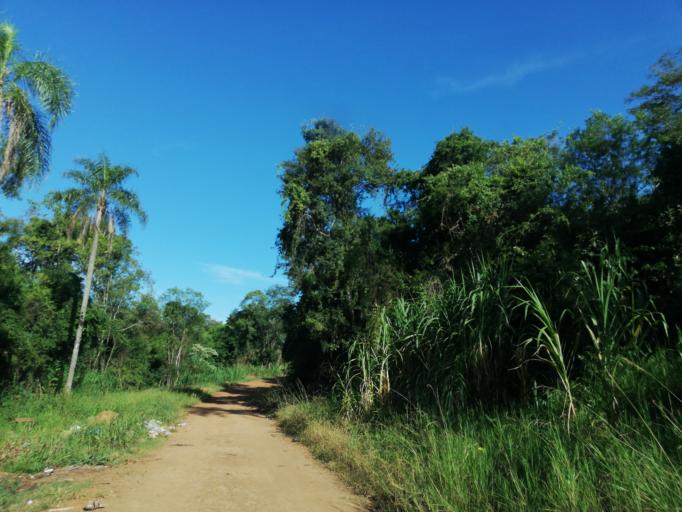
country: AR
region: Misiones
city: Dos de Mayo
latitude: -26.9893
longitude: -54.4956
